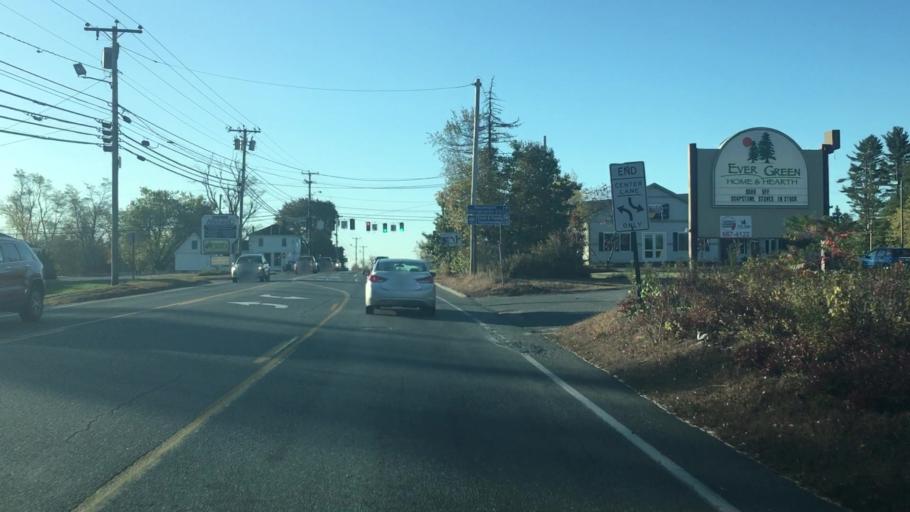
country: US
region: Maine
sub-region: Hancock County
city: Ellsworth
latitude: 44.5203
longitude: -68.3963
